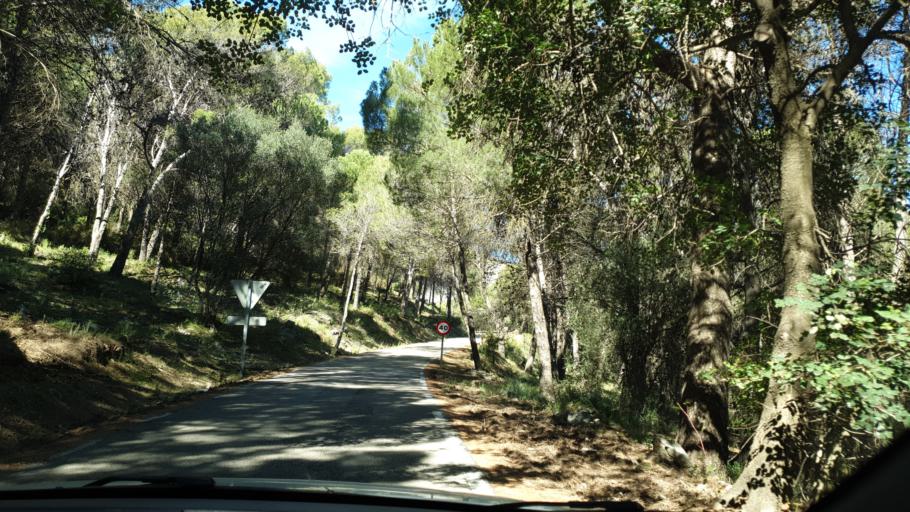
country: ES
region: Andalusia
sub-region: Provincia de Malaga
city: Ojen
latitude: 36.5921
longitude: -4.8532
